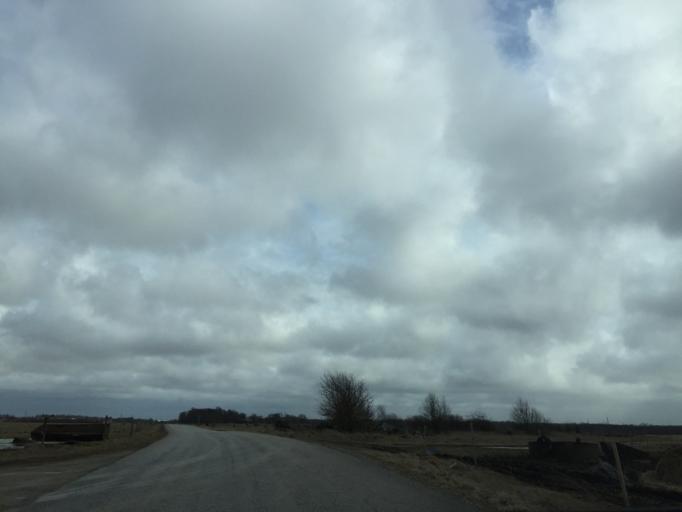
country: EE
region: Laeaene
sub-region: Lihula vald
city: Lihula
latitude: 58.7283
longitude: 23.8868
